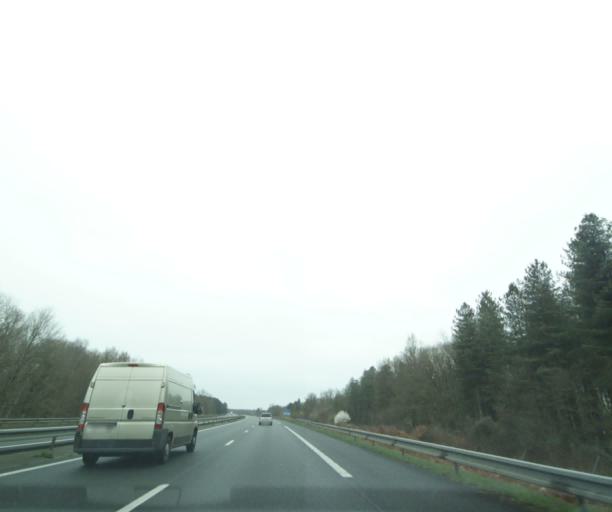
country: FR
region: Centre
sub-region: Departement du Loir-et-Cher
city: Nouan-le-Fuzelier
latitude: 47.5233
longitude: 2.0044
